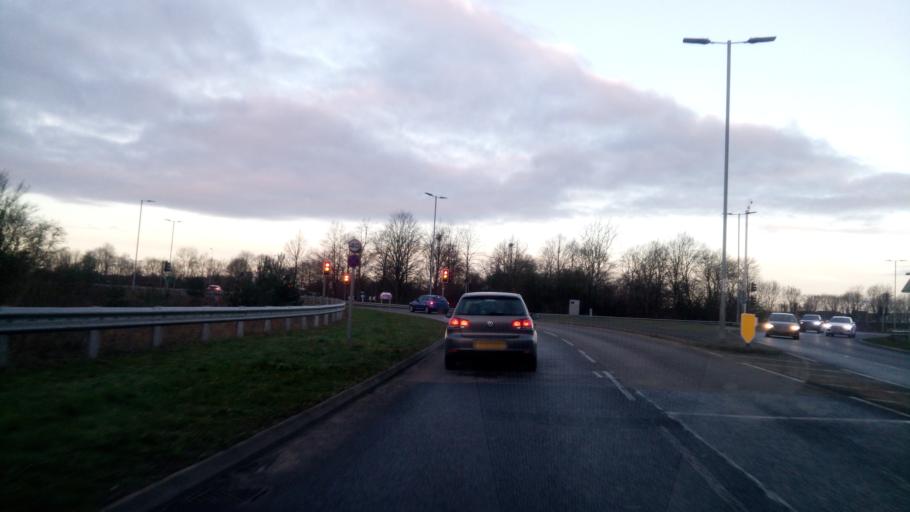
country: GB
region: England
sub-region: Peterborough
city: Peterborough
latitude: 52.5873
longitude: -0.2790
